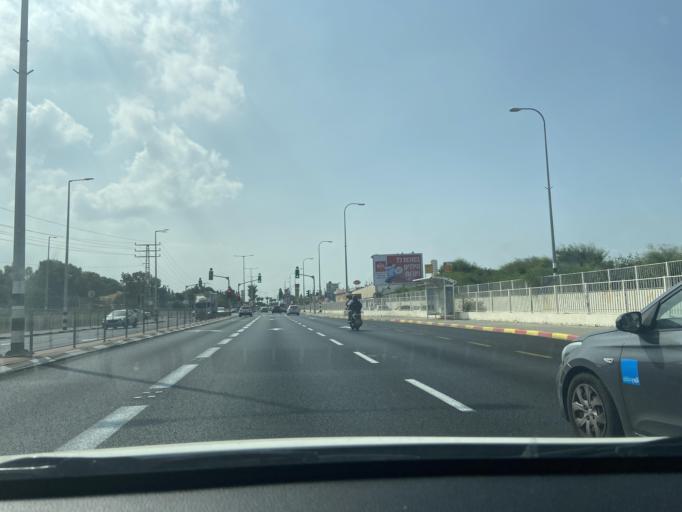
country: IL
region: Northern District
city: El Mazra`a
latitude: 32.9949
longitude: 35.0972
